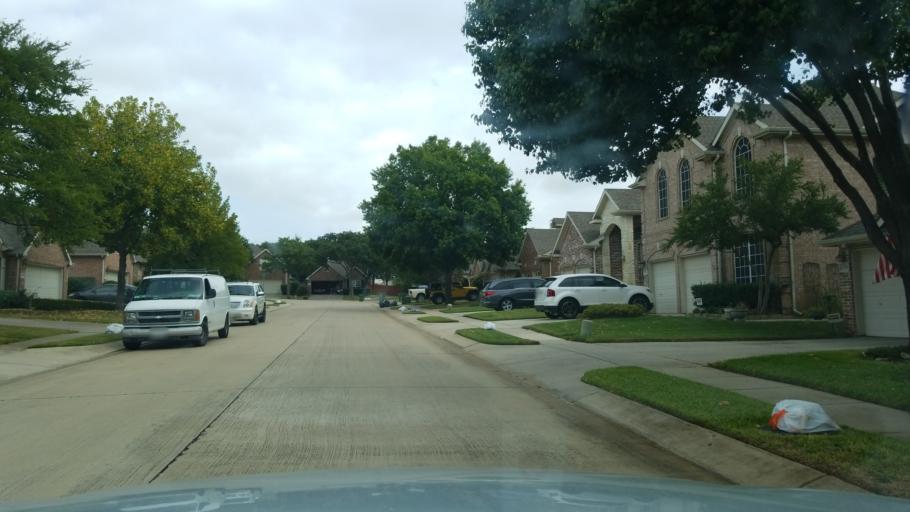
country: US
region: Texas
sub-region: Tarrant County
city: Euless
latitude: 32.8417
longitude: -97.1040
